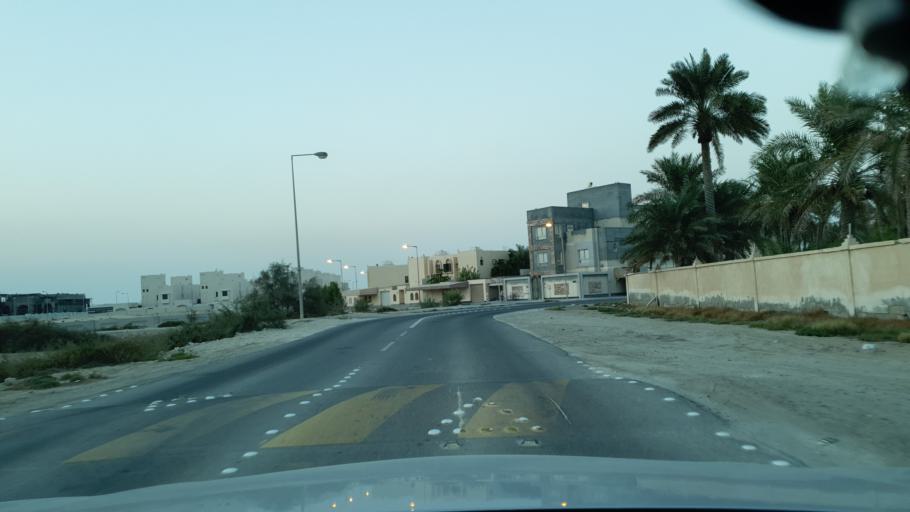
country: BH
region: Central Governorate
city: Dar Kulayb
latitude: 25.9771
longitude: 50.6147
